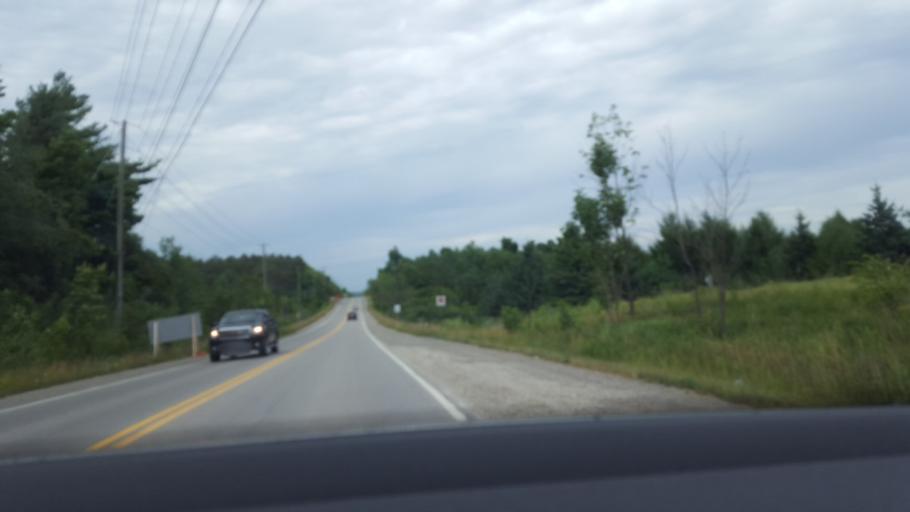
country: CA
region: Ontario
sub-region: Halton
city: Milton
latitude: 43.5067
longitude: -79.9593
